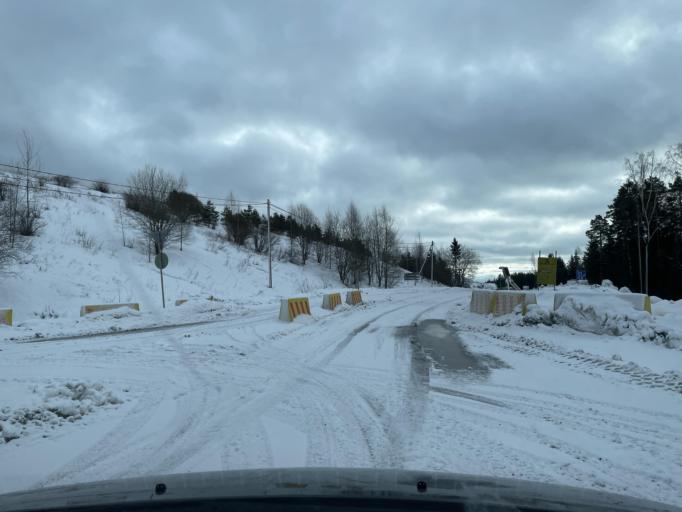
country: FI
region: Uusimaa
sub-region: Helsinki
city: Espoo
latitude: 60.2376
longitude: 24.5555
